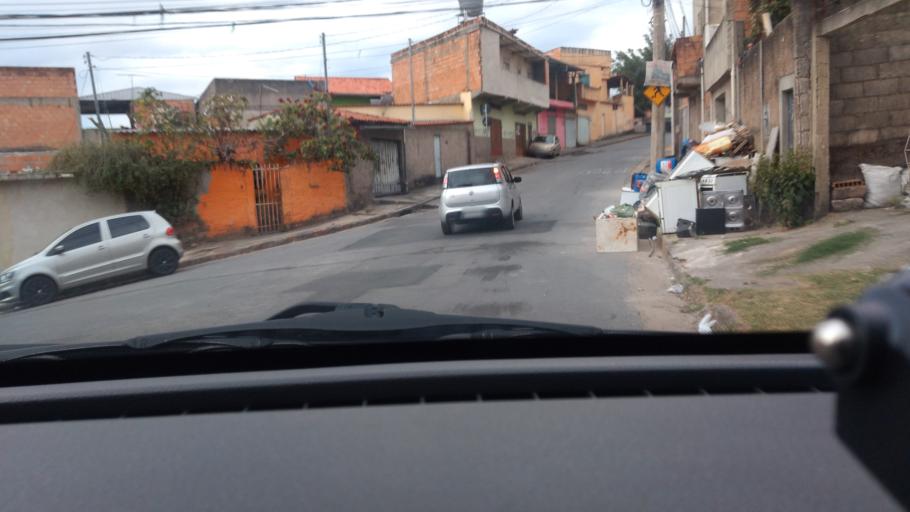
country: BR
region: Minas Gerais
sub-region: Santa Luzia
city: Santa Luzia
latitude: -19.8142
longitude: -43.9387
